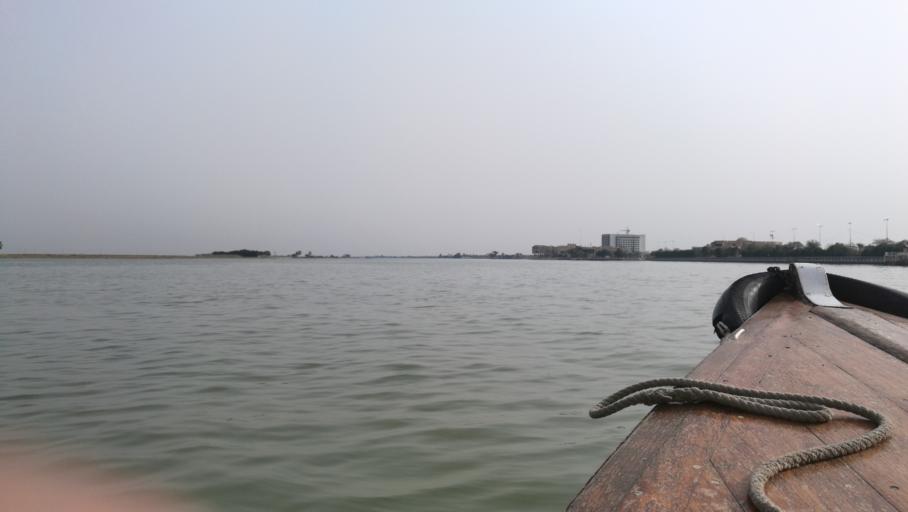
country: IQ
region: Basra Governorate
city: Al Basrah al Qadimah
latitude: 30.5033
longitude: 47.8584
